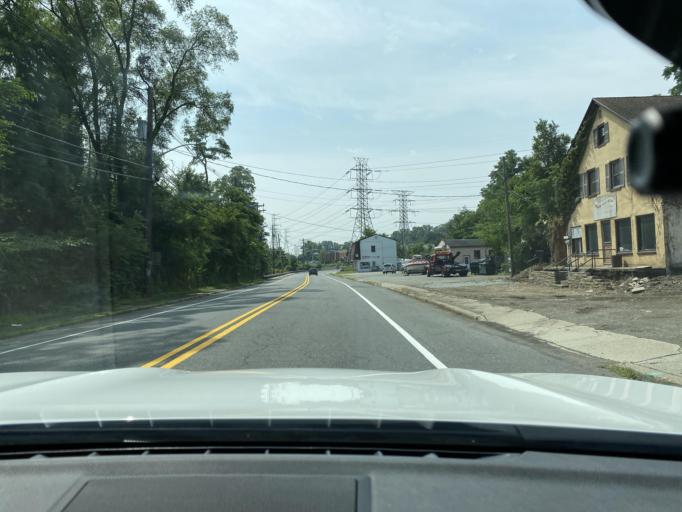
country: US
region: New York
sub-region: Rockland County
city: Suffern
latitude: 41.1055
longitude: -74.1511
